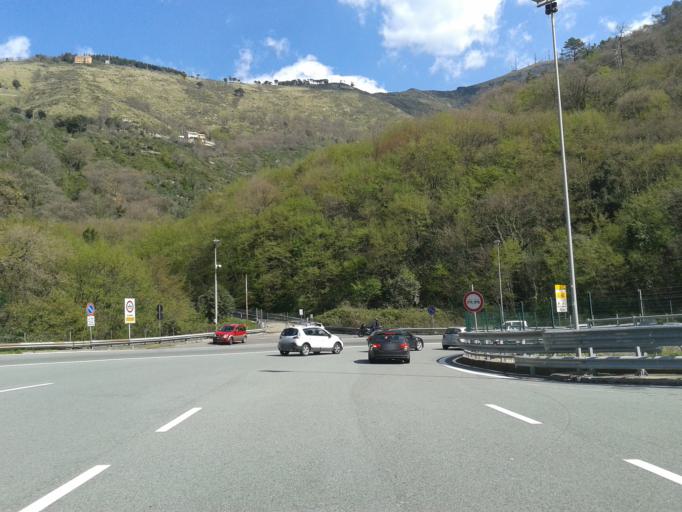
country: IT
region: Liguria
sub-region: Provincia di Genova
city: Bogliasco
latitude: 44.3977
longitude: 9.0146
